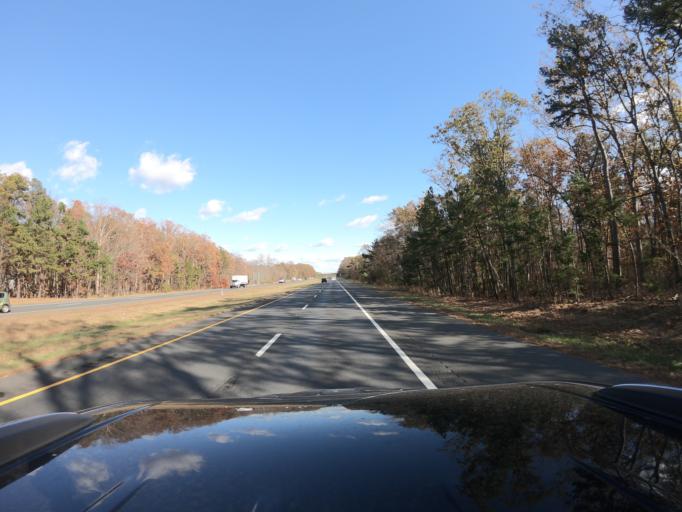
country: US
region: New Jersey
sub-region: Monmouth County
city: Farmingdale
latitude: 40.1669
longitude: -74.2049
